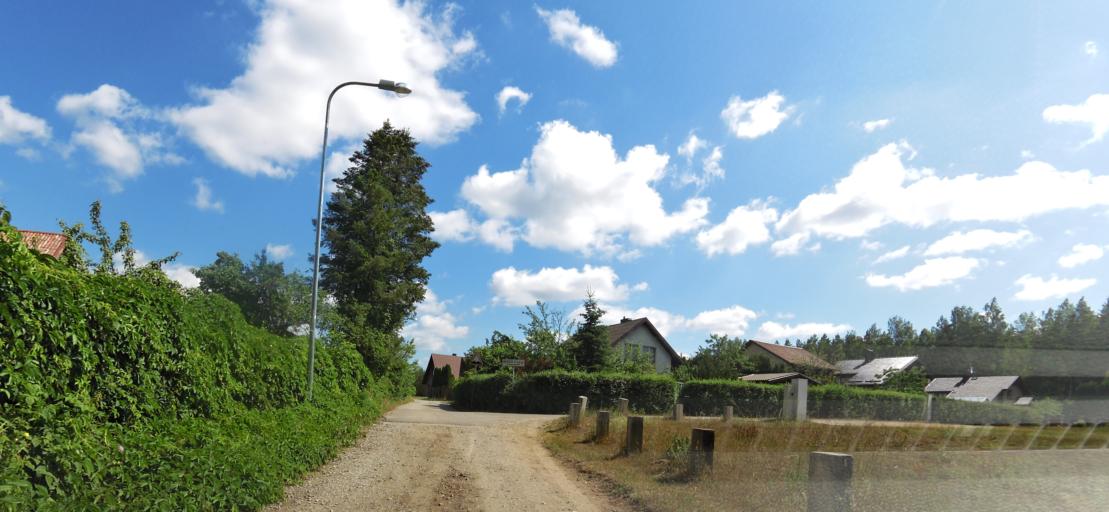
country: LT
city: Nemencine
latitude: 54.8190
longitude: 25.3925
